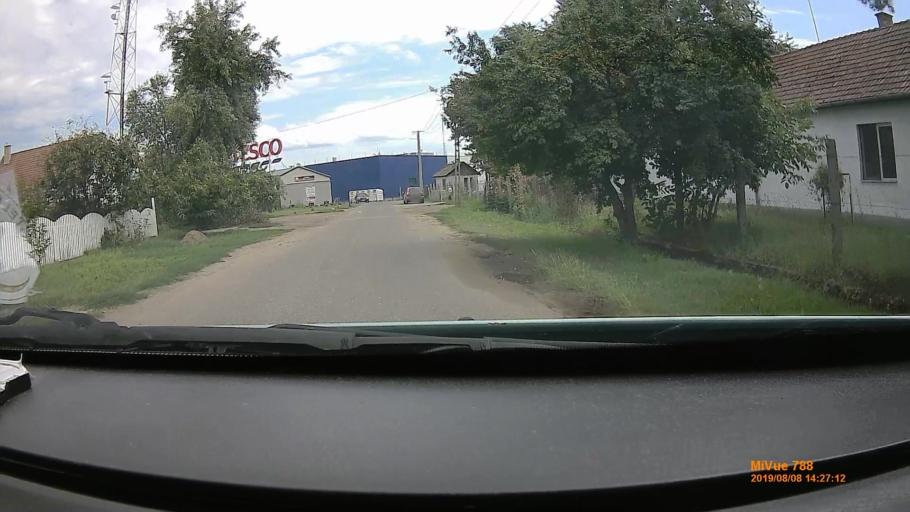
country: HU
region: Szabolcs-Szatmar-Bereg
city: Mateszalka
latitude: 47.9472
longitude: 22.3221
